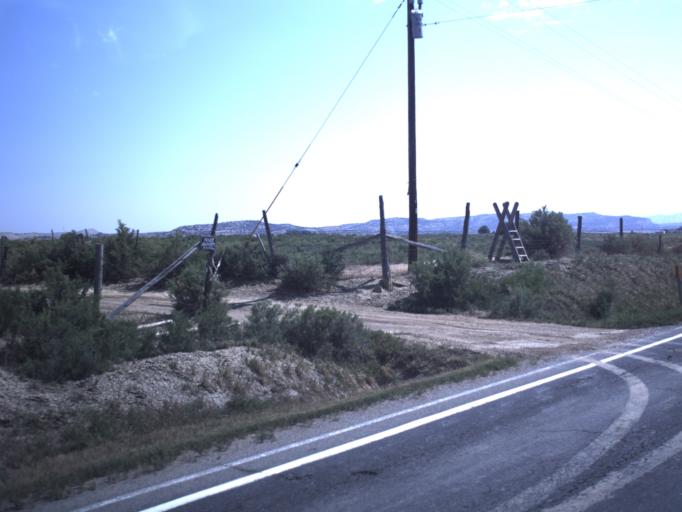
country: US
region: Utah
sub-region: Daggett County
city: Manila
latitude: 40.9885
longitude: -109.6993
